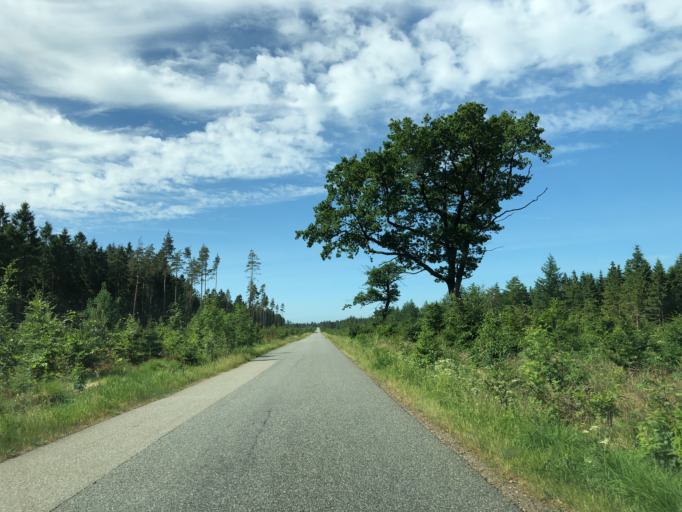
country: DK
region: Central Jutland
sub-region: Herning Kommune
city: Kibaek
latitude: 56.0515
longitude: 8.9265
